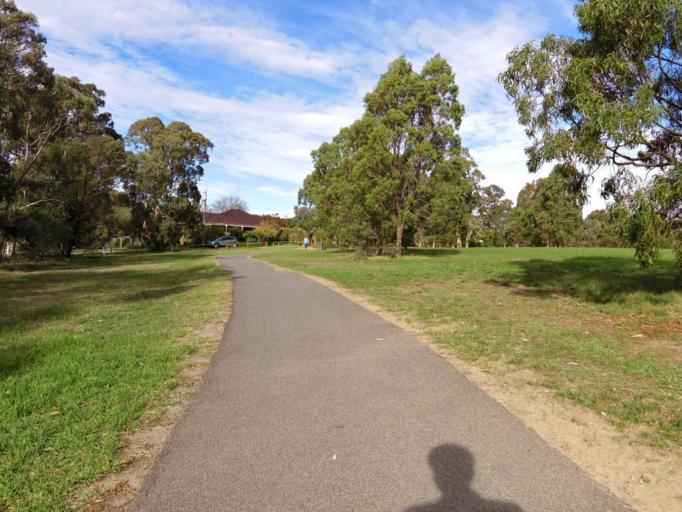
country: AU
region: Victoria
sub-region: Manningham
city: Doncaster East
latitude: -37.7729
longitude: 145.1395
